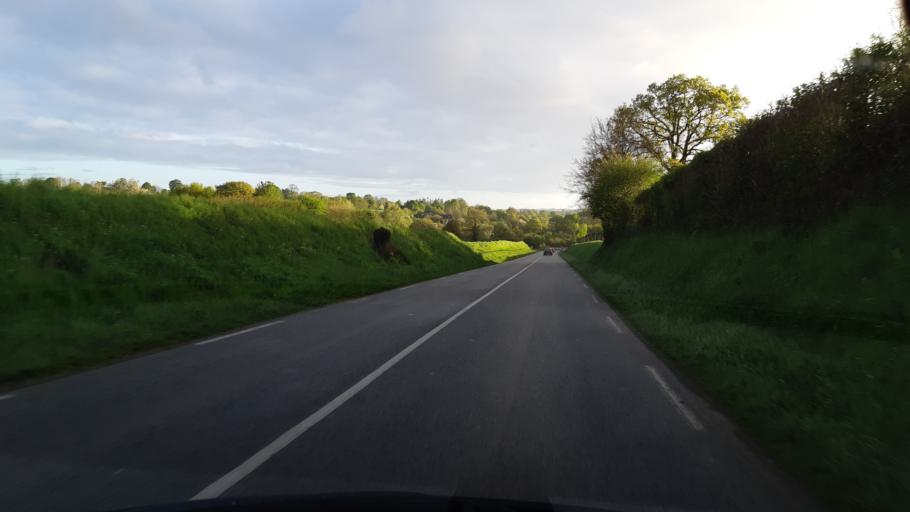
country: FR
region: Lower Normandy
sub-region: Departement de la Manche
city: Agneaux
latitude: 49.0658
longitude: -1.1323
